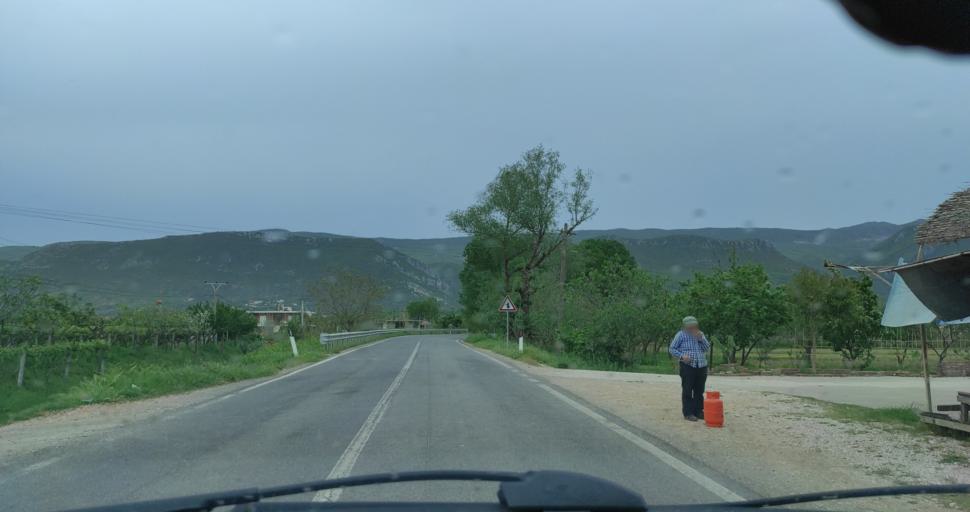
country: AL
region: Lezhe
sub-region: Rrethi i Kurbinit
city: Mamurras
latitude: 41.6015
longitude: 19.7026
